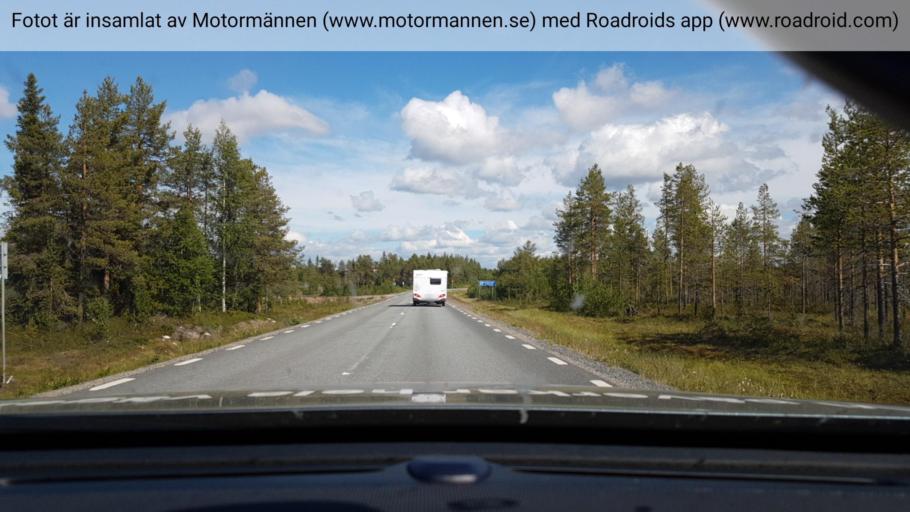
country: SE
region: Norrbotten
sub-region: Arjeplogs Kommun
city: Arjeplog
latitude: 65.5848
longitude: 18.1474
